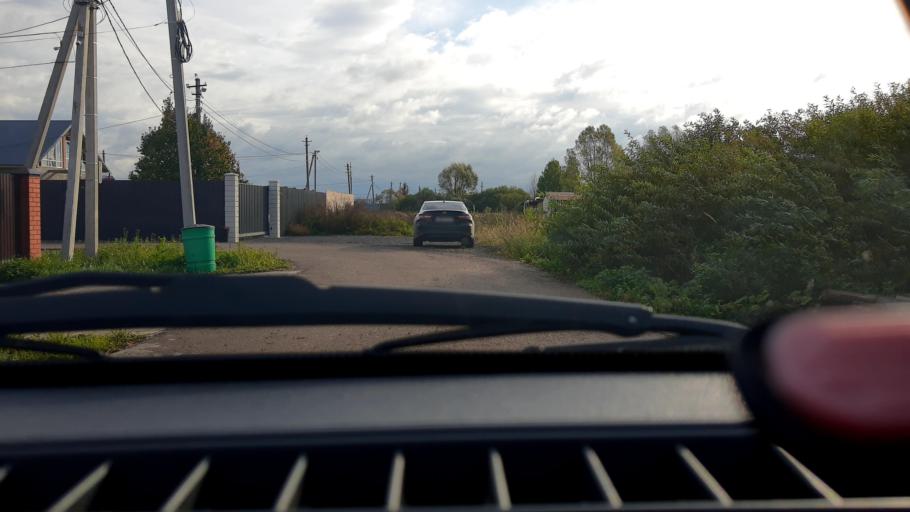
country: RU
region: Bashkortostan
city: Kabakovo
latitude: 54.6566
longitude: 56.1891
